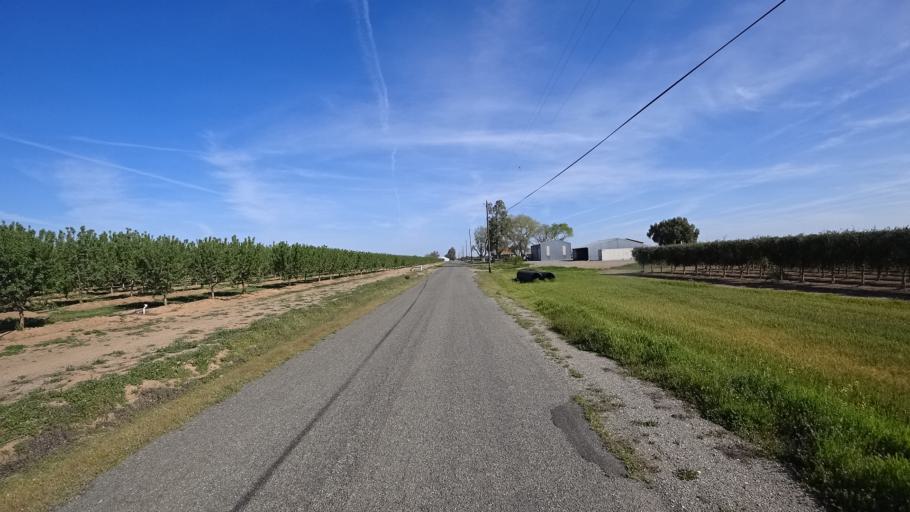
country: US
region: California
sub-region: Glenn County
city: Willows
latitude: 39.6304
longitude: -122.2160
